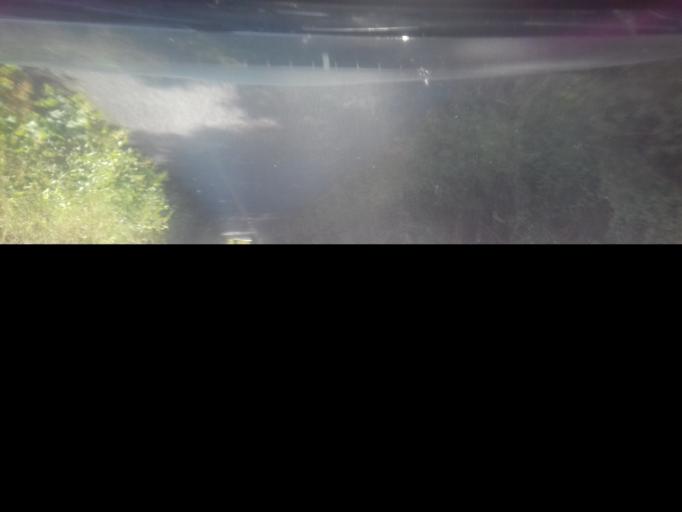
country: IE
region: Leinster
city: Hartstown
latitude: 53.4231
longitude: -6.4190
